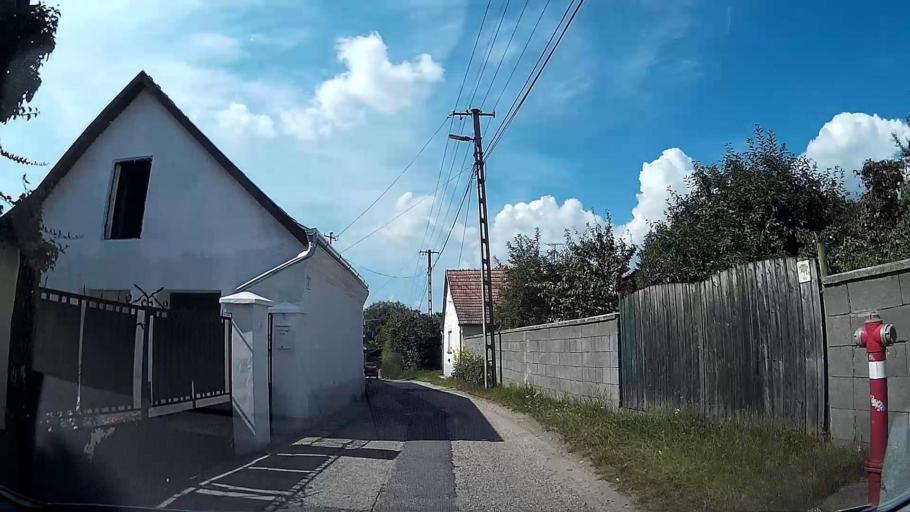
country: HU
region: Pest
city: Tahitotfalu
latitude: 47.7530
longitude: 19.0902
